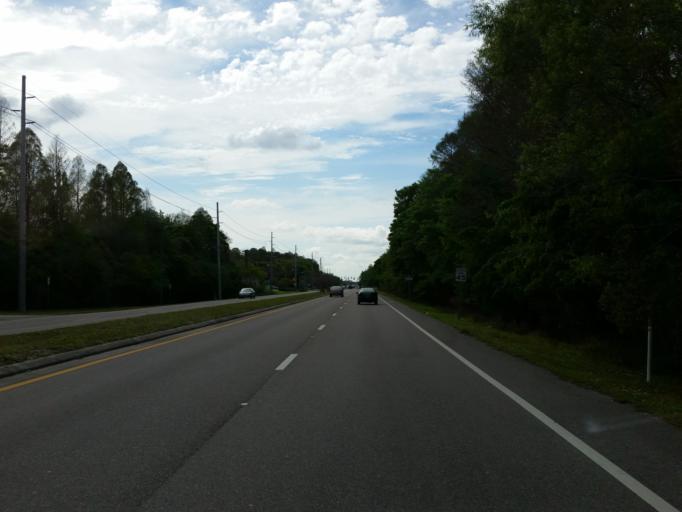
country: US
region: Florida
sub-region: Hillsborough County
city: Temple Terrace
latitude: 28.0693
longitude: -82.3978
